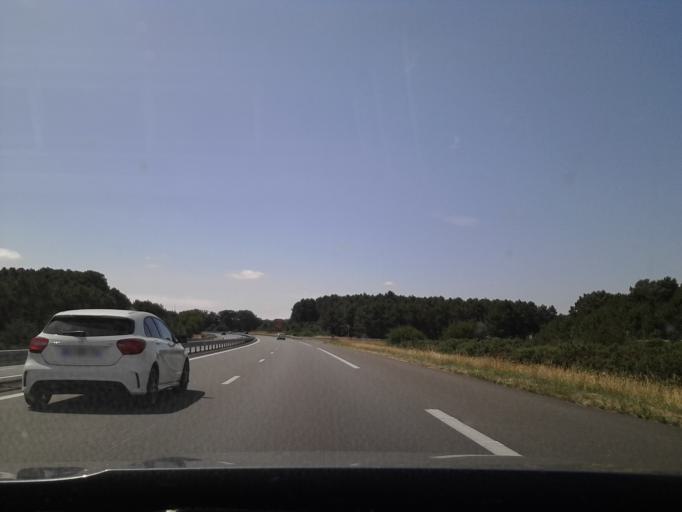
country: FR
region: Pays de la Loire
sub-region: Departement de la Sarthe
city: Teloche
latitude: 47.8600
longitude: 0.2978
